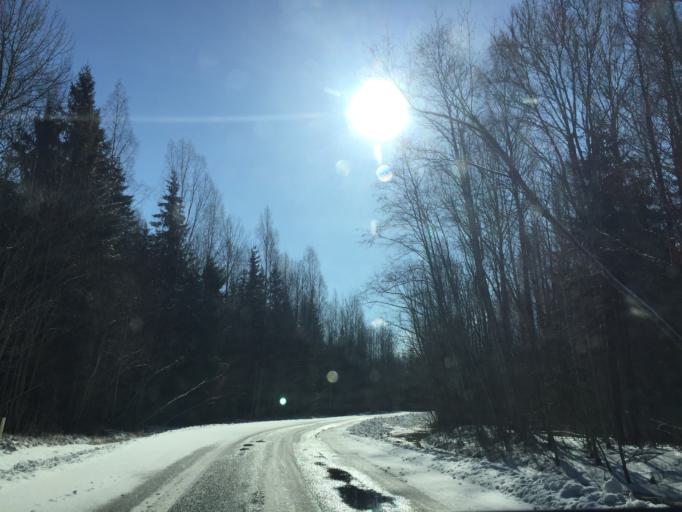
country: LV
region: Salacgrivas
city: Ainazi
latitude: 58.0074
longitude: 24.5007
